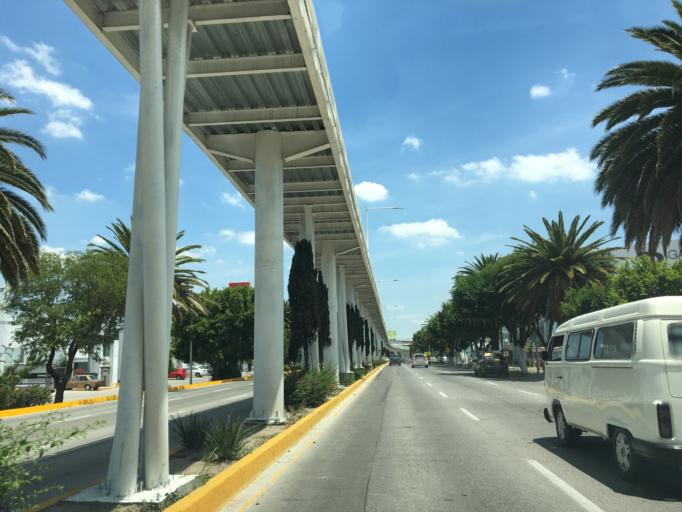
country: MX
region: Puebla
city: Puebla
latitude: 19.0691
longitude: -98.2252
